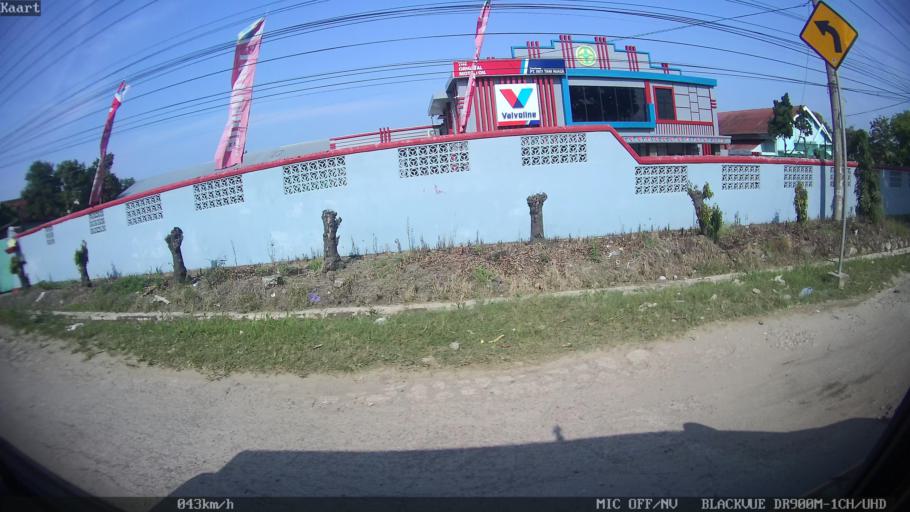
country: ID
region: Lampung
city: Natar
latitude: -5.2778
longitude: 105.1882
